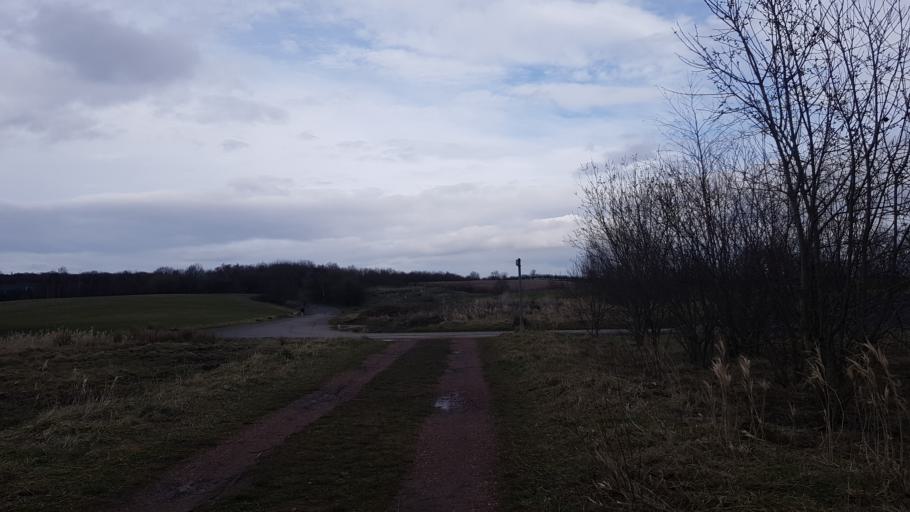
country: GB
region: England
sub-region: City and Borough of Leeds
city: Swillington
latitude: 53.7493
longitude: -1.3956
